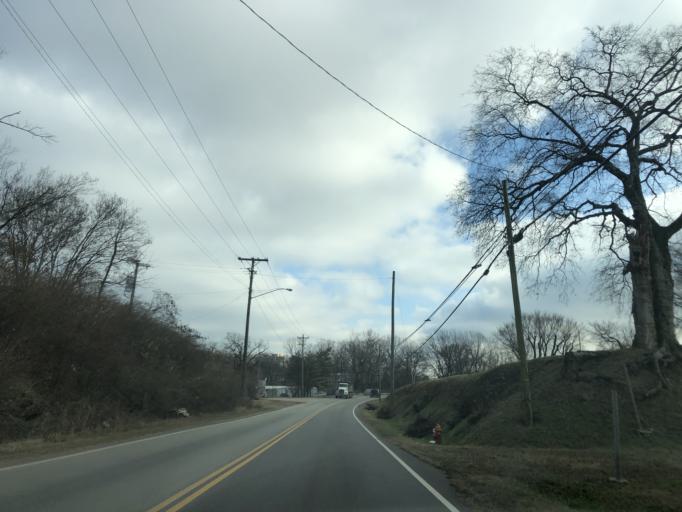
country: US
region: Tennessee
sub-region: Davidson County
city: Nashville
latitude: 36.1999
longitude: -86.7858
